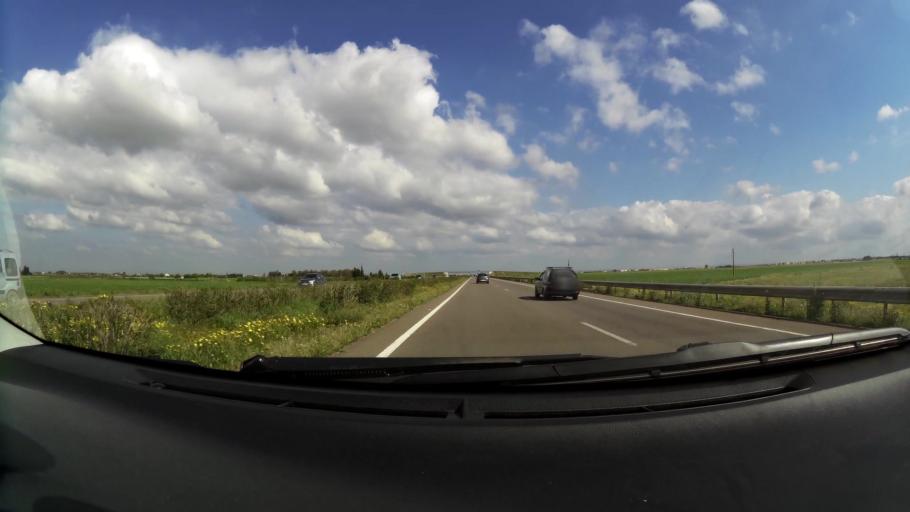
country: MA
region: Chaouia-Ouardigha
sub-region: Settat Province
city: Berrechid
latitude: 33.3096
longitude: -7.5899
